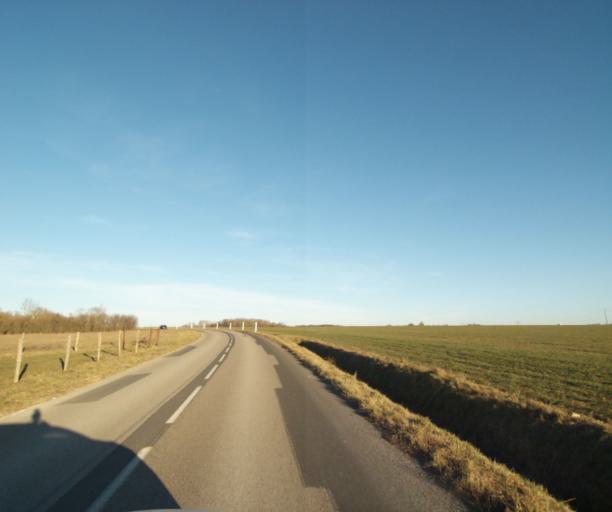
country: FR
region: Lorraine
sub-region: Departement de Meurthe-et-Moselle
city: Art-sur-Meurthe
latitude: 48.6603
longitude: 6.2740
